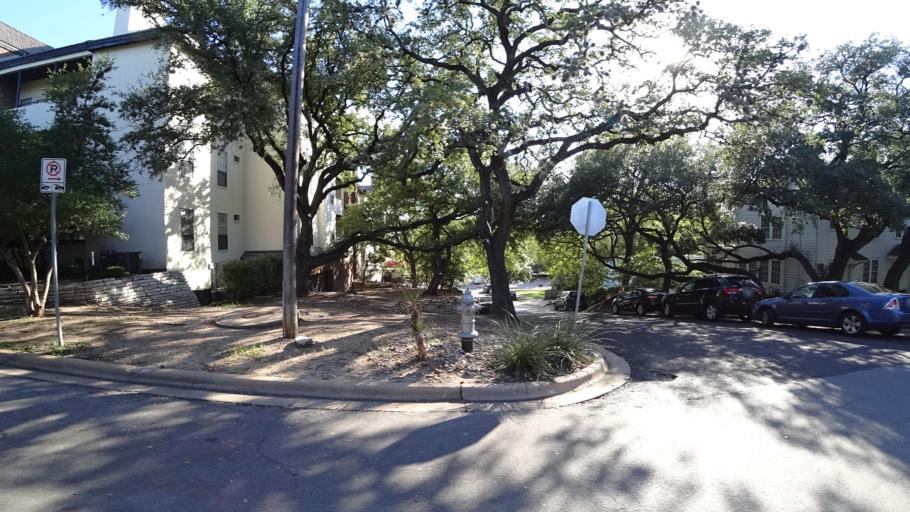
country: US
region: Texas
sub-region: Travis County
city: Austin
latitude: 30.2956
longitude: -97.7378
